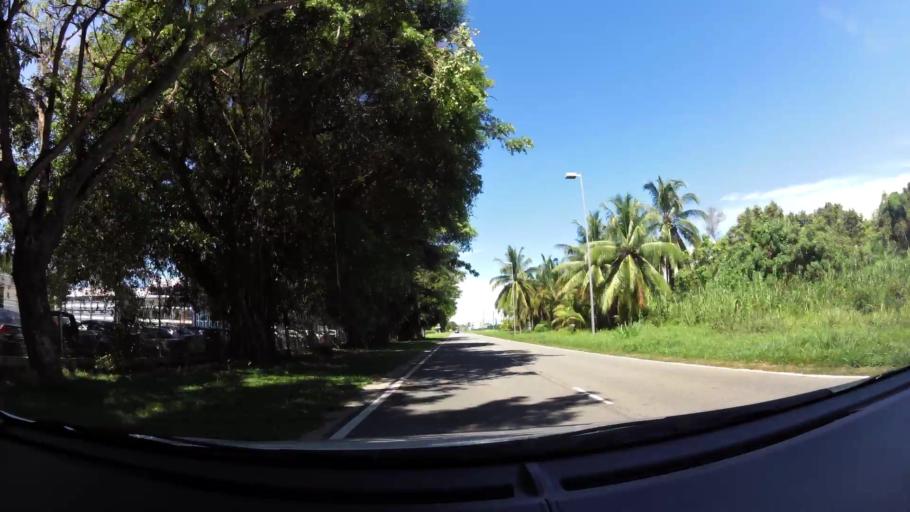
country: BN
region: Brunei and Muara
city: Bandar Seri Begawan
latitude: 5.0336
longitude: 115.0743
